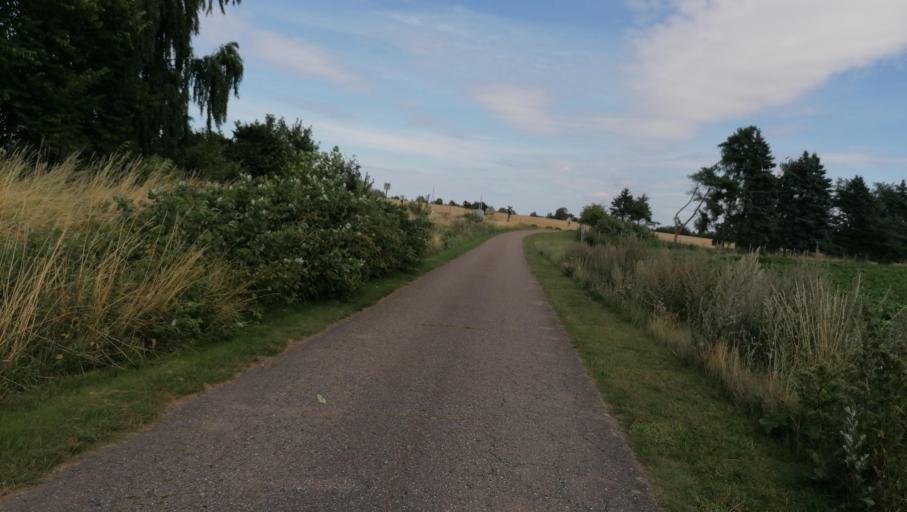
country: DK
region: Zealand
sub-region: Odsherred Kommune
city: Horve
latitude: 55.7581
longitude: 11.4598
